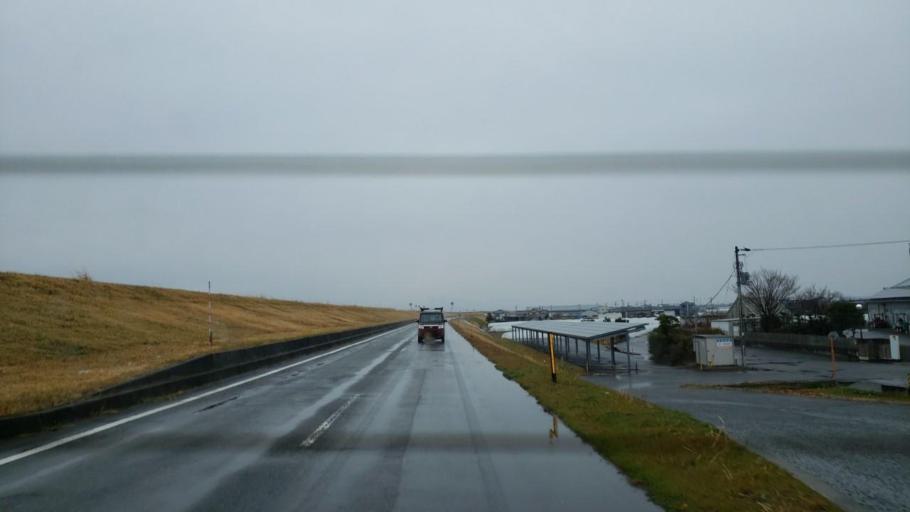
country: JP
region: Tokushima
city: Ishii
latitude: 34.1004
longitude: 134.4148
